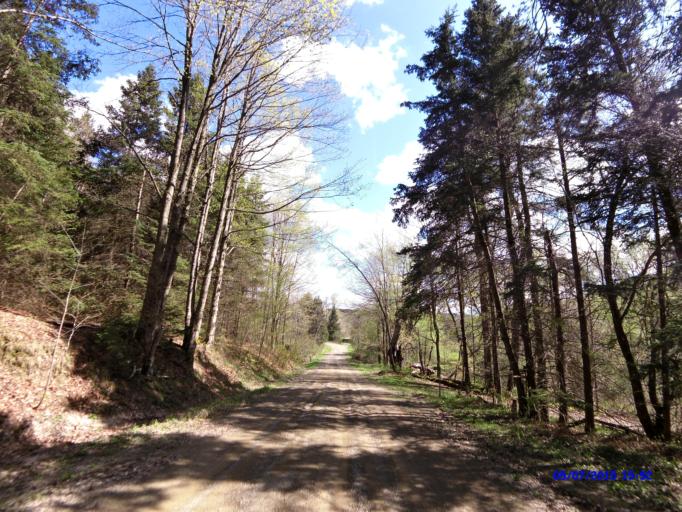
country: US
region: New York
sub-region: Cattaraugus County
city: Franklinville
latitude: 42.3260
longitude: -78.5419
